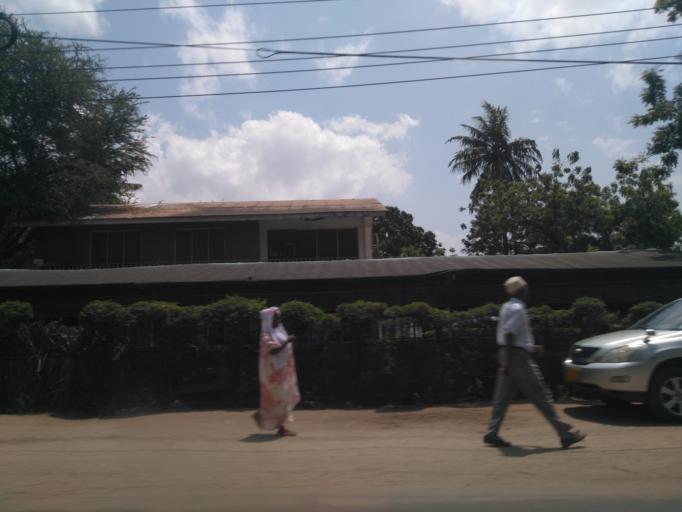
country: TZ
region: Dar es Salaam
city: Dar es Salaam
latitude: -6.8069
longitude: 39.2750
